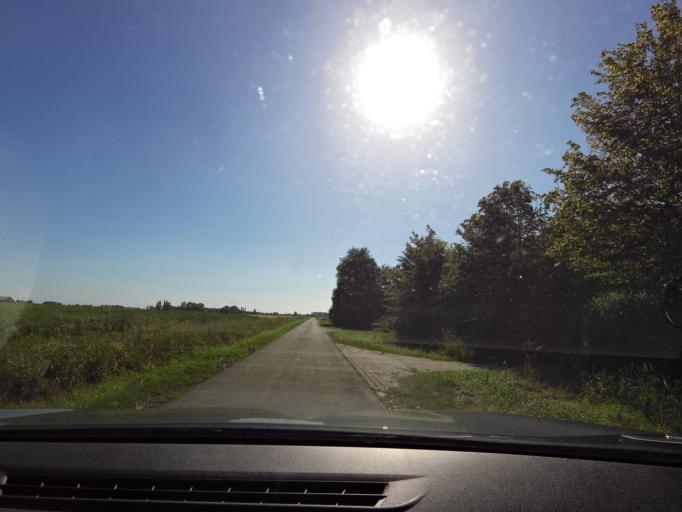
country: NL
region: South Holland
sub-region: Gemeente Hellevoetsluis
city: Nieuwenhoorn
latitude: 51.8704
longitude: 4.1395
